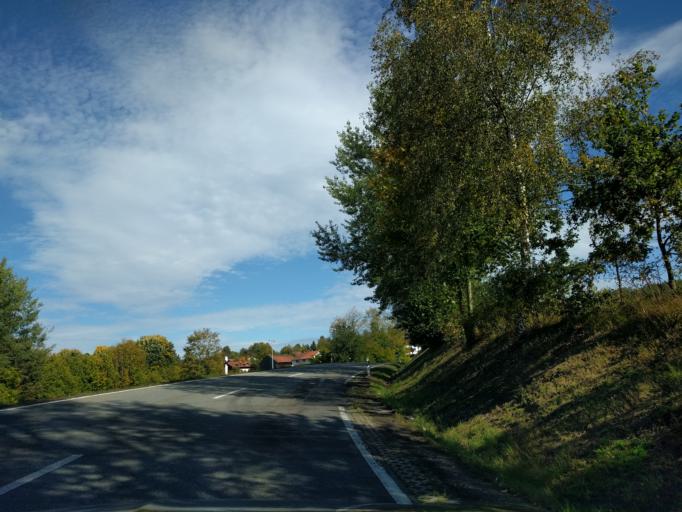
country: DE
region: Bavaria
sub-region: Upper Palatinate
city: Kotzting
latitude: 49.1387
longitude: 12.8871
